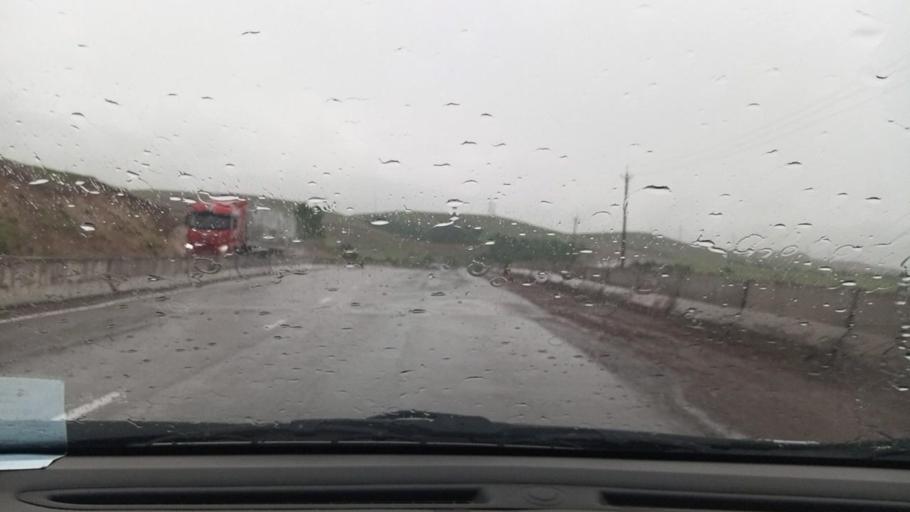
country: UZ
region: Toshkent
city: Angren
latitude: 41.0573
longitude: 70.1682
